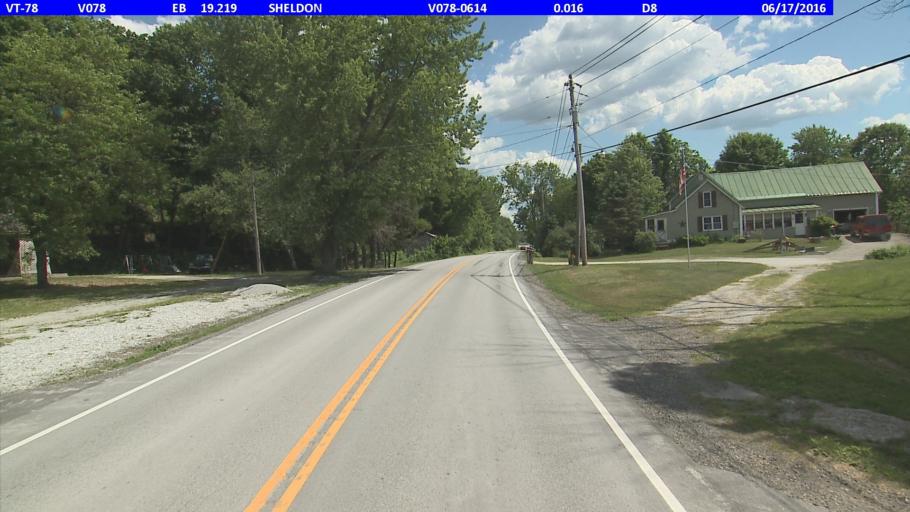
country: US
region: Vermont
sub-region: Franklin County
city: Swanton
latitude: 44.9243
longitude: -72.9675
